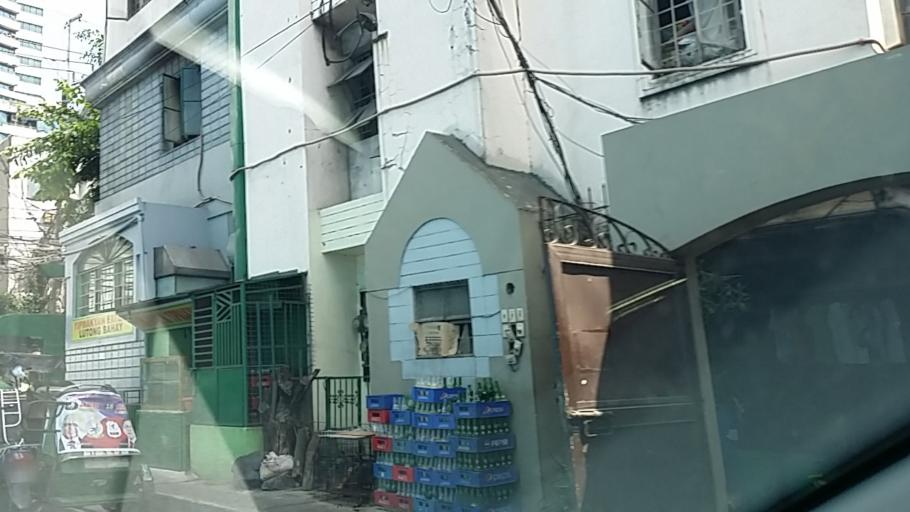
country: PH
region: Metro Manila
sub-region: Mandaluyong
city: Mandaluyong City
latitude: 14.5771
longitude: 121.0494
